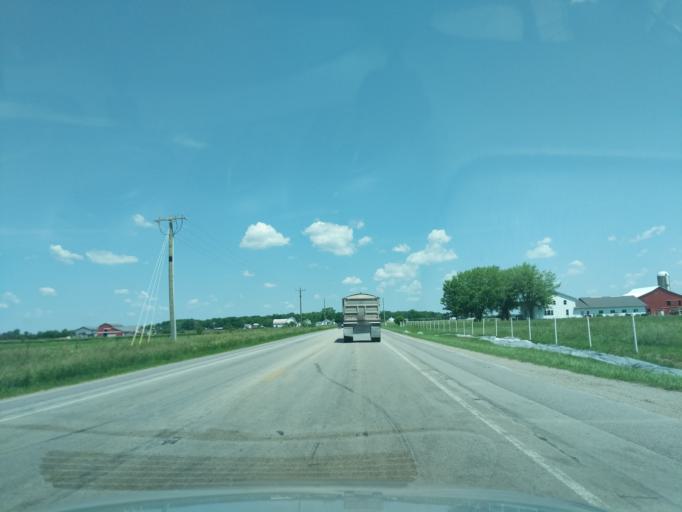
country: US
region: Indiana
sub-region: LaGrange County
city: Topeka
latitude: 41.5535
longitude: -85.5782
